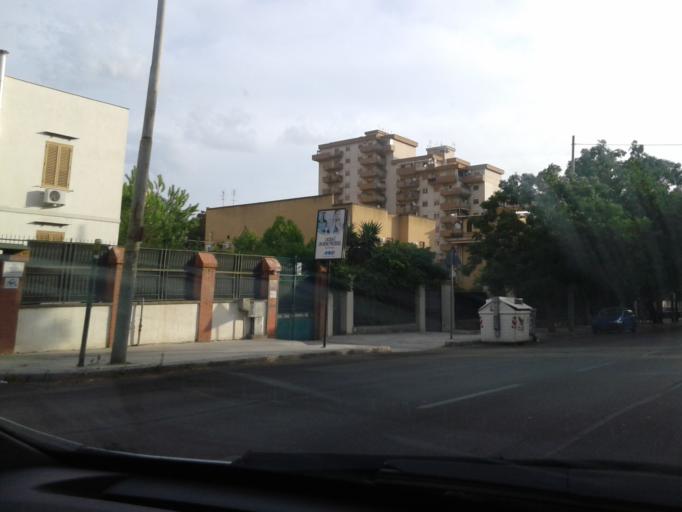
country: IT
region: Sicily
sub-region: Palermo
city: Monreale
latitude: 38.0959
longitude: 13.3126
